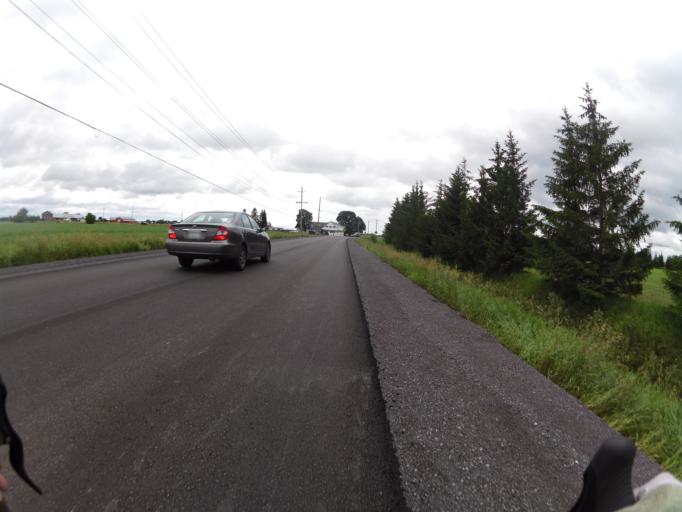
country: CA
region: Ontario
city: Bells Corners
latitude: 45.2386
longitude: -75.8744
